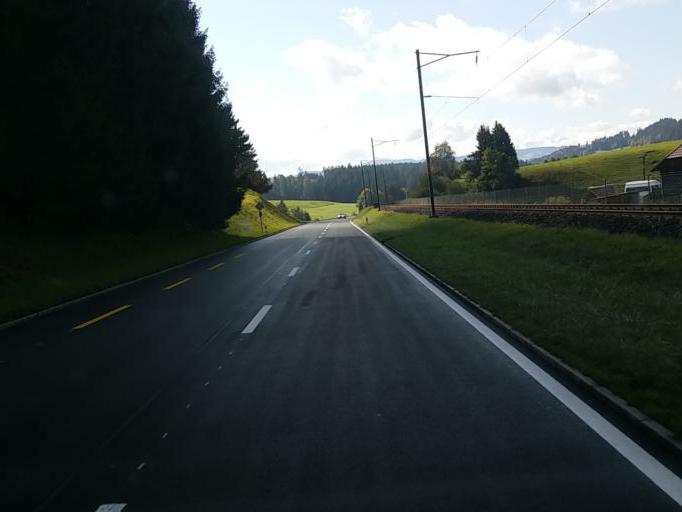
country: CH
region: Bern
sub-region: Emmental District
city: Sumiswald
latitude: 47.0523
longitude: 7.7494
